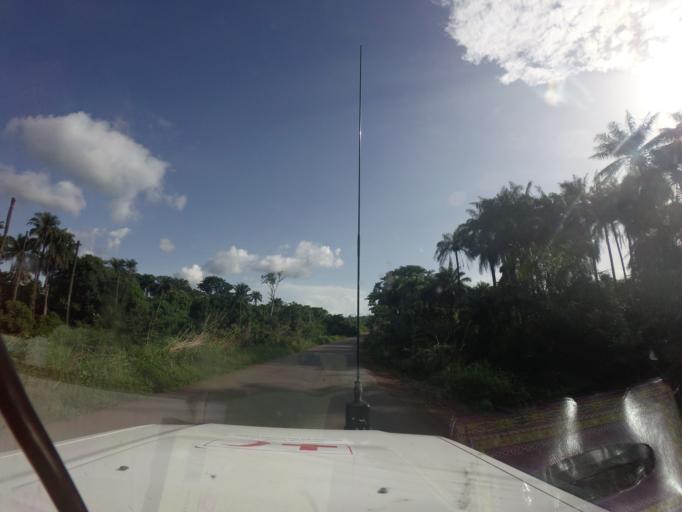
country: GN
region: Kindia
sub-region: Kindia
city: Kindia
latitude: 10.1104
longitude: -12.5639
